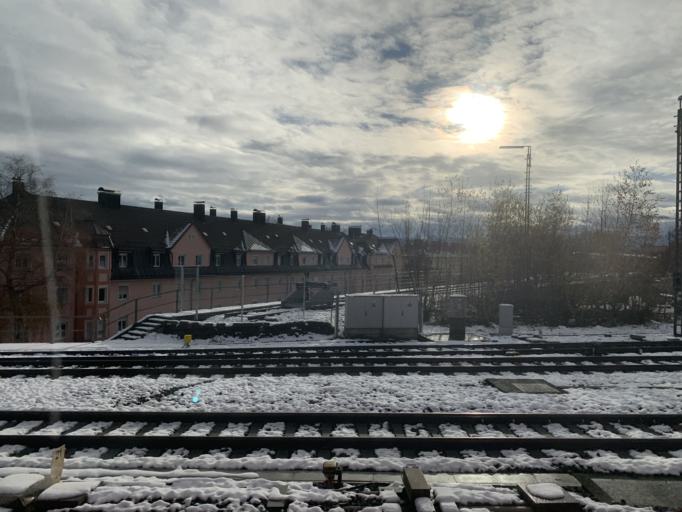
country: DE
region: Bavaria
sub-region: Swabia
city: Kempten (Allgaeu)
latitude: 47.7140
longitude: 10.3197
